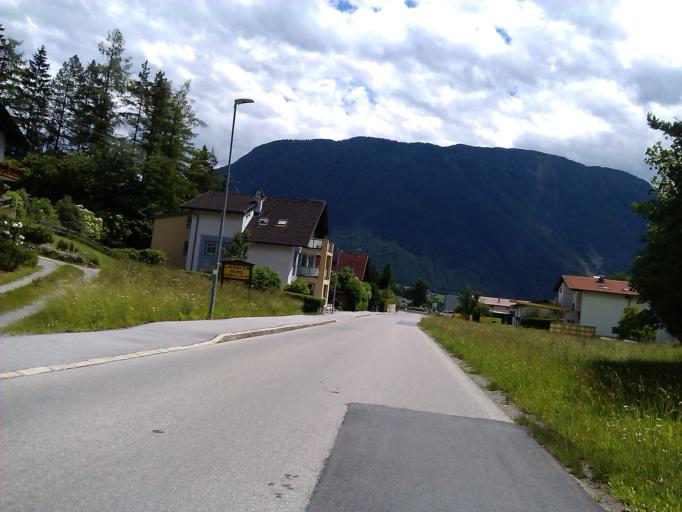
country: AT
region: Tyrol
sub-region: Politischer Bezirk Imst
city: Nassereith
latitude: 47.3195
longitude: 10.8302
